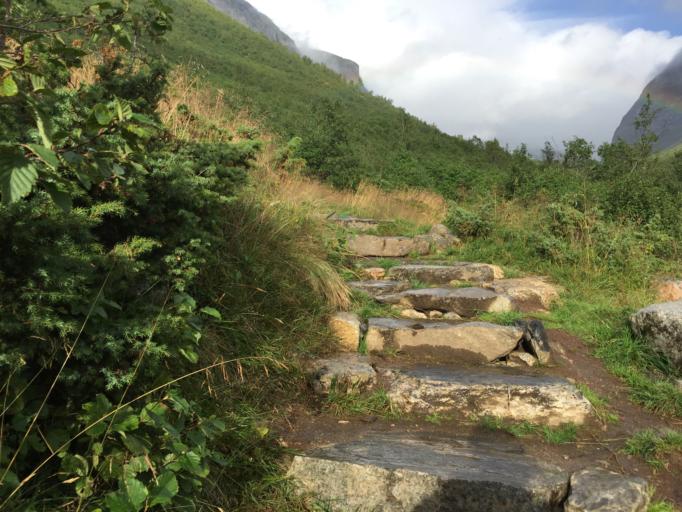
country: NO
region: More og Romsdal
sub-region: Norddal
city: Valldal
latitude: 62.1034
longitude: 7.2224
